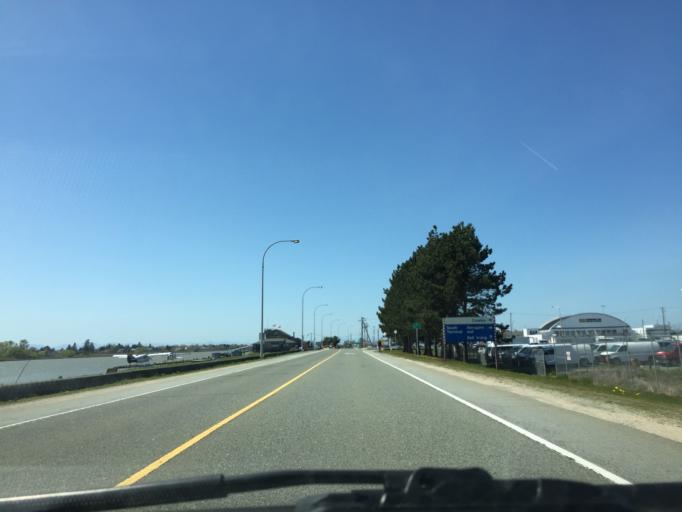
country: CA
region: British Columbia
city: Richmond
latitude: 49.1777
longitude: -123.1645
